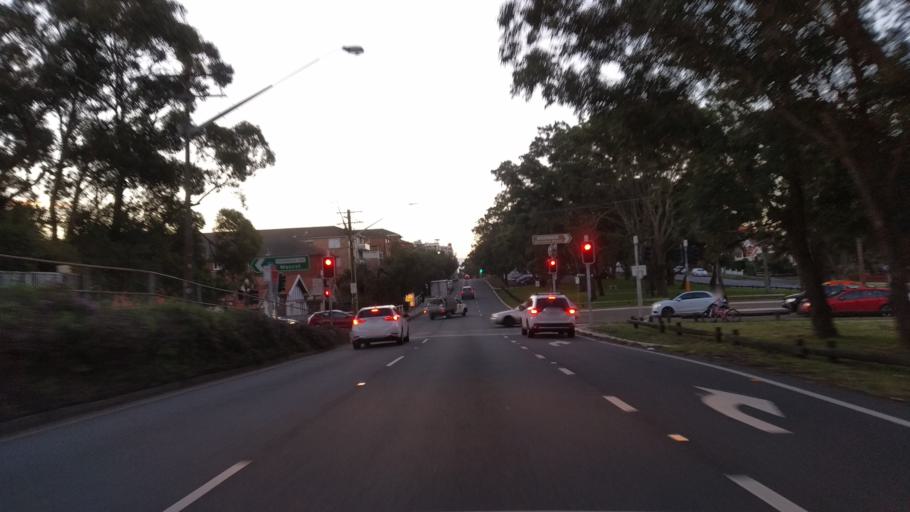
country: AU
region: New South Wales
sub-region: Randwick
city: Maroubra
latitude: -33.9465
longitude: 151.2403
